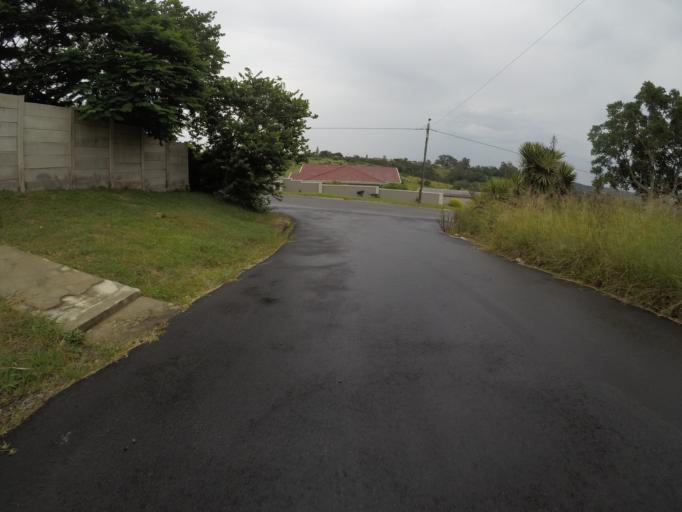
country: ZA
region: Eastern Cape
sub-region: Buffalo City Metropolitan Municipality
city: East London
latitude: -32.9646
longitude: 27.8440
